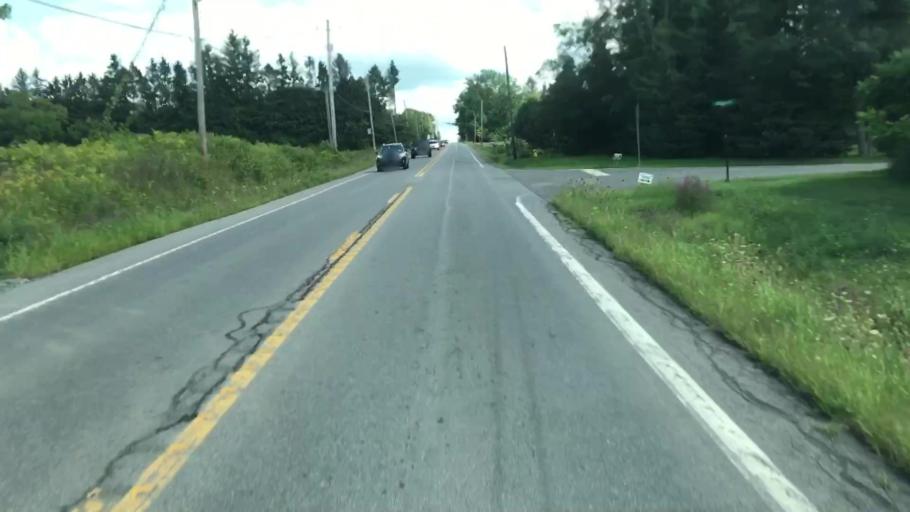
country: US
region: New York
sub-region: Onondaga County
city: Marcellus
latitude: 42.9837
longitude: -76.3116
